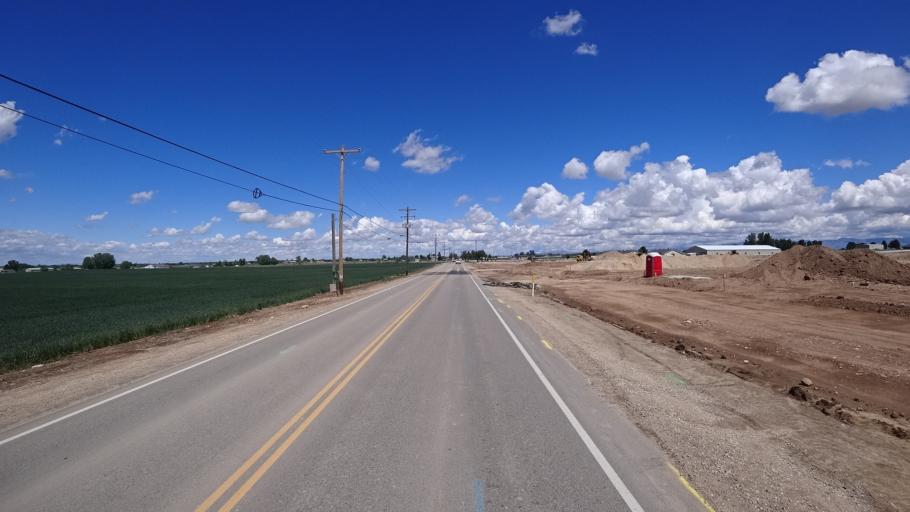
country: US
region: Idaho
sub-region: Ada County
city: Kuna
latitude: 43.5141
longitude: -116.4337
